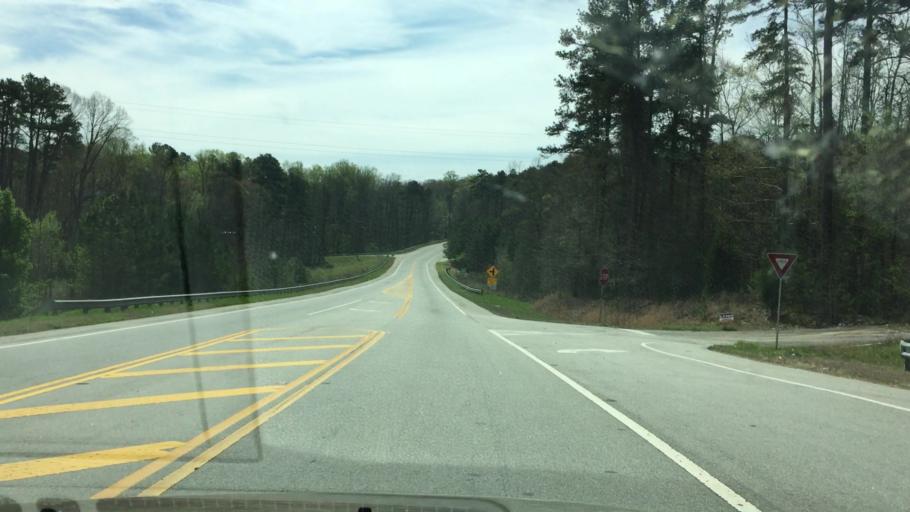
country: US
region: Georgia
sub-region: Barrow County
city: Winder
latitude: 34.0311
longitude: -83.7135
